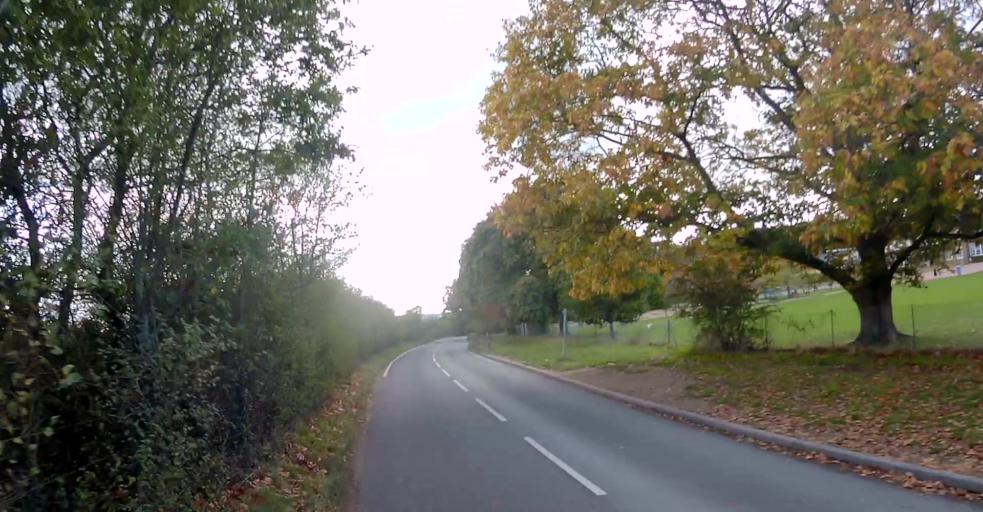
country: GB
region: England
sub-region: Surrey
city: Elstead
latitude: 51.1912
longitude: -0.7468
